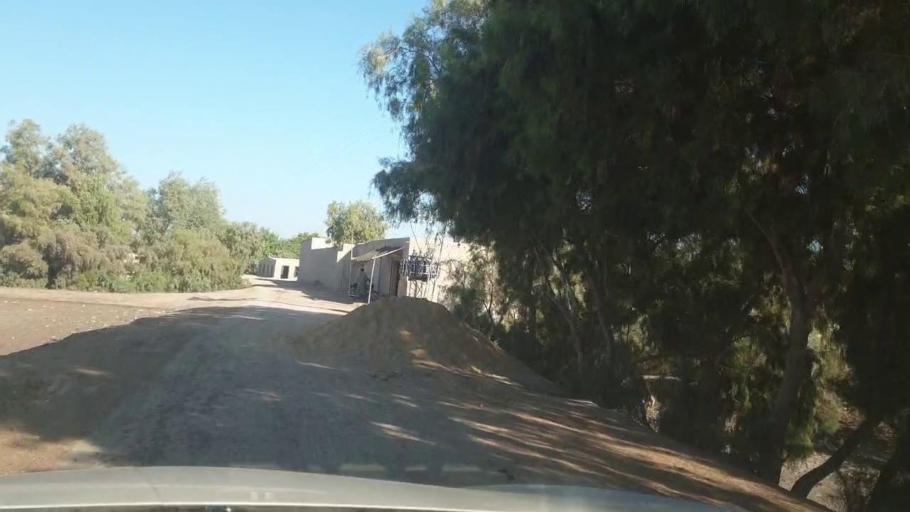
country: PK
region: Sindh
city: Bhan
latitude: 26.5368
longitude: 67.6743
